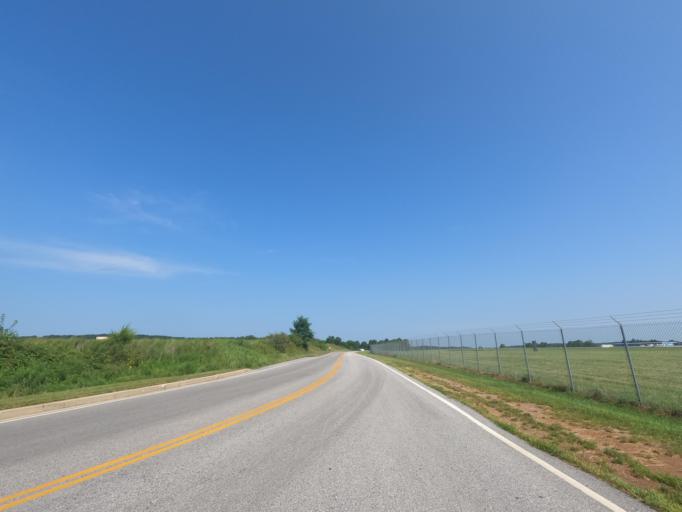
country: US
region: Maryland
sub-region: Carroll County
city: Westminster
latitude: 39.6021
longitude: -77.0057
